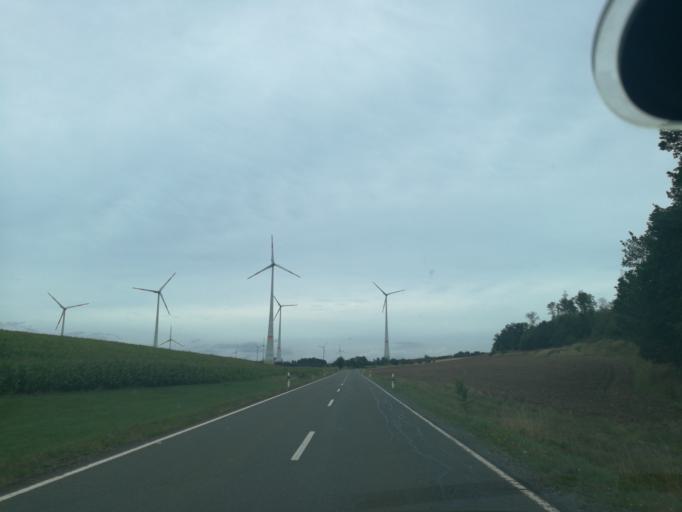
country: DE
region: Bavaria
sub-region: Upper Franconia
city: Gattendorf
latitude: 50.2984
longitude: 12.0117
